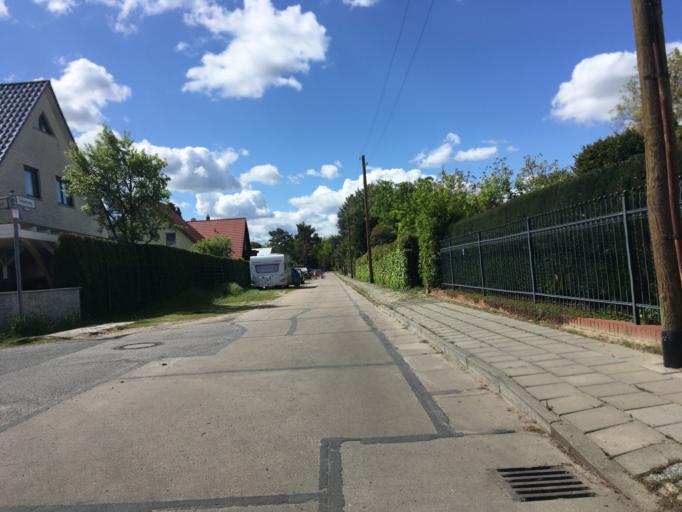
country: DE
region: Berlin
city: Bohnsdorf
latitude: 52.3914
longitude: 13.5692
